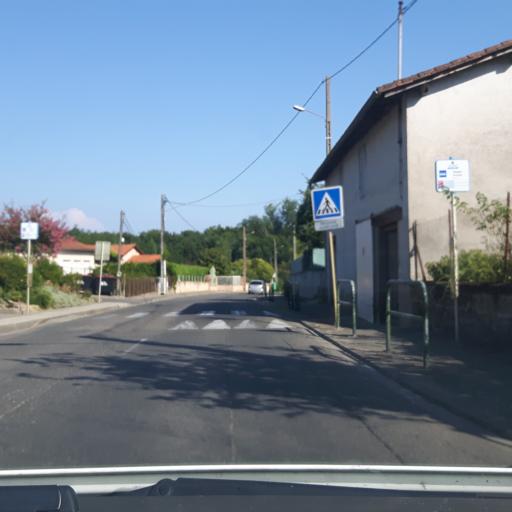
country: FR
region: Midi-Pyrenees
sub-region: Departement de la Haute-Garonne
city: Fronton
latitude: 43.8389
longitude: 1.3921
